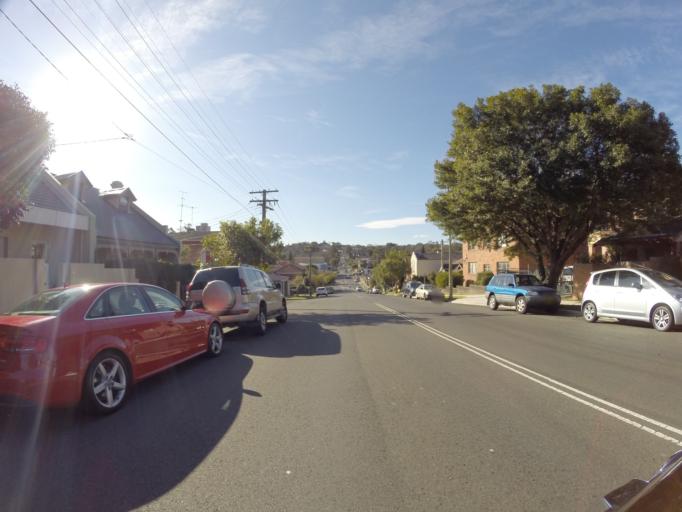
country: AU
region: New South Wales
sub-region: Randwick
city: Randwick
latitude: -33.9185
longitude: 151.2485
